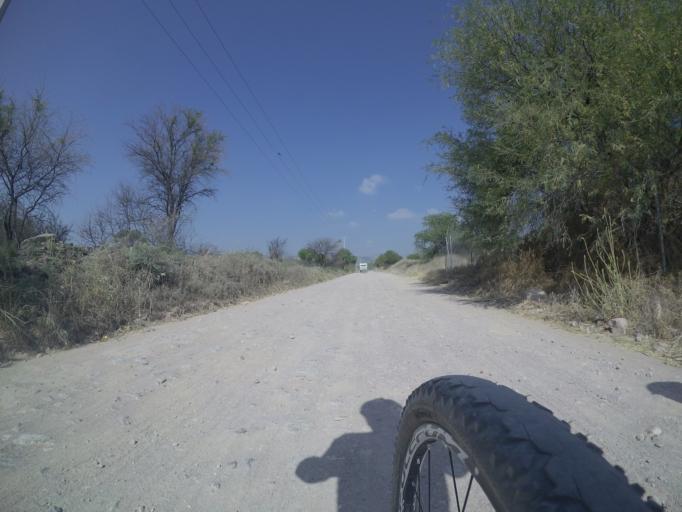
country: MX
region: Aguascalientes
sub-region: Jesus Maria
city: Paseos de las Haciendas [Fraccionamiento]
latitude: 21.9987
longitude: -102.3407
